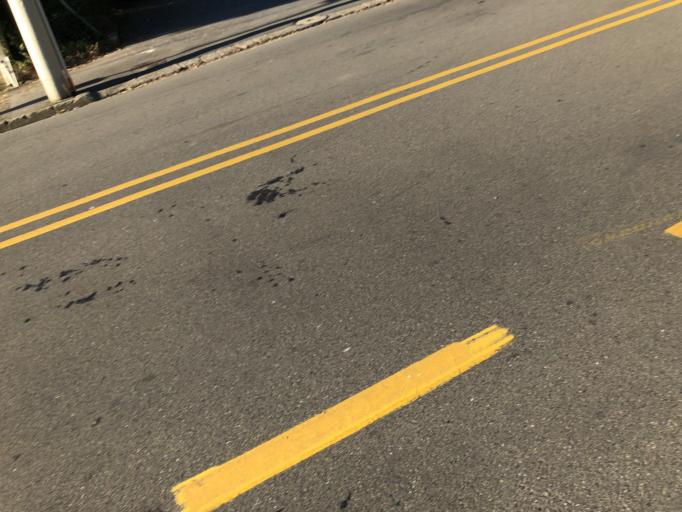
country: NZ
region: Wellington
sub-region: Wellington City
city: Wellington
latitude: -41.2991
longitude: 174.7882
